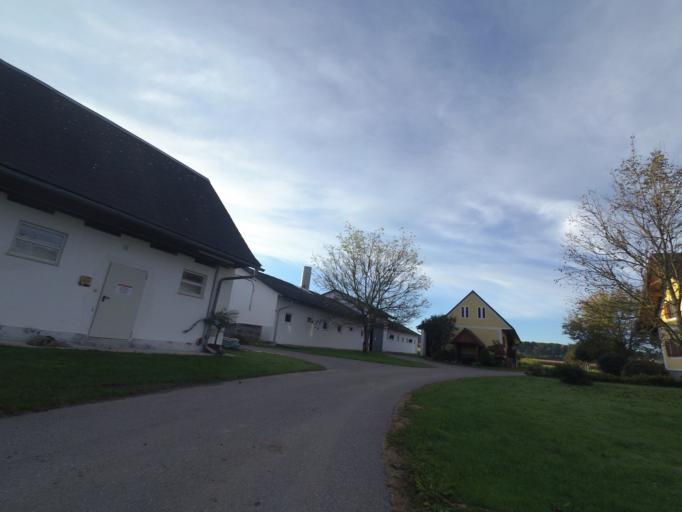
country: AT
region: Styria
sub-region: Politischer Bezirk Deutschlandsberg
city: Sankt Martin im Sulmtal
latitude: 46.7529
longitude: 15.2909
